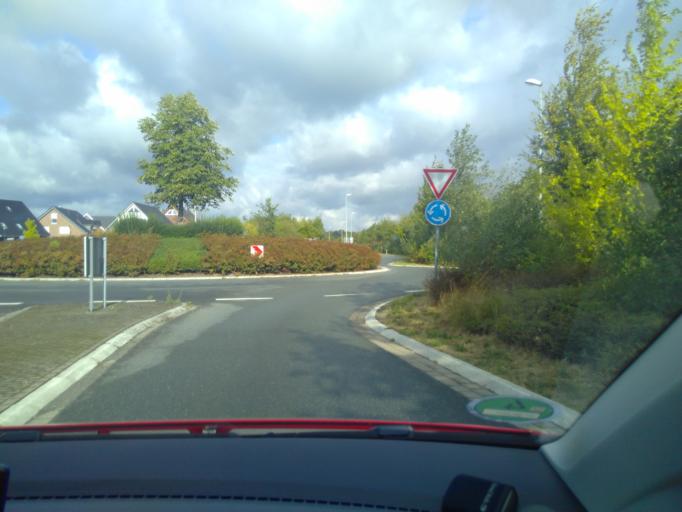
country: DE
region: North Rhine-Westphalia
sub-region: Regierungsbezirk Munster
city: Warendorf
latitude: 51.9621
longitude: 8.0049
